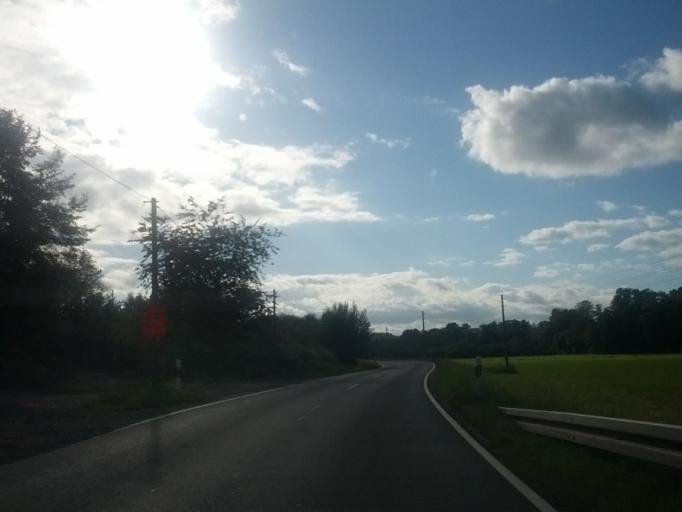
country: DE
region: Thuringia
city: Marksuhl
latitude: 50.9490
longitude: 10.2013
